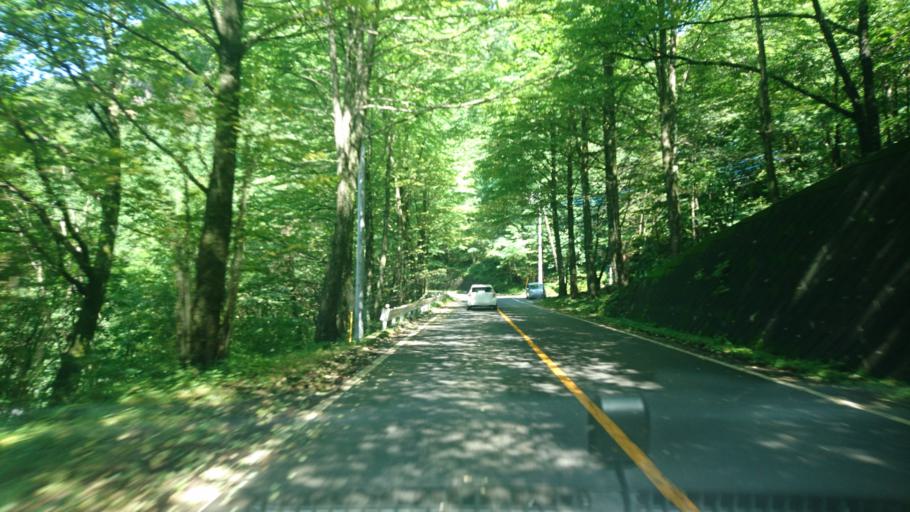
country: JP
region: Nagano
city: Saku
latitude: 36.2986
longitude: 138.6536
